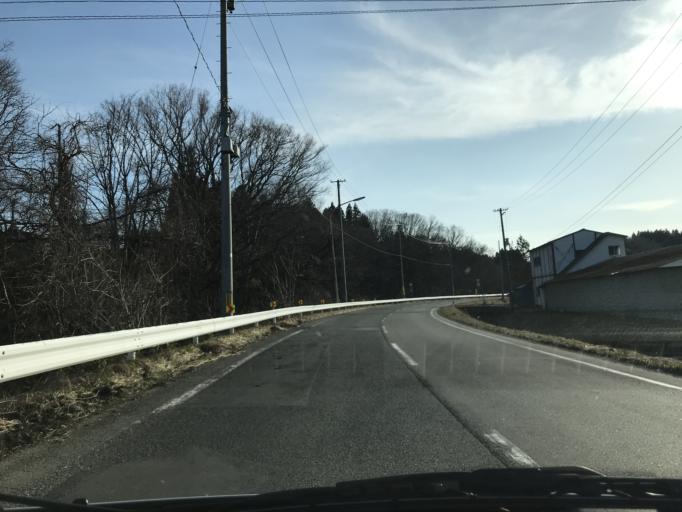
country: JP
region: Iwate
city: Kitakami
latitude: 39.2410
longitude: 141.1000
